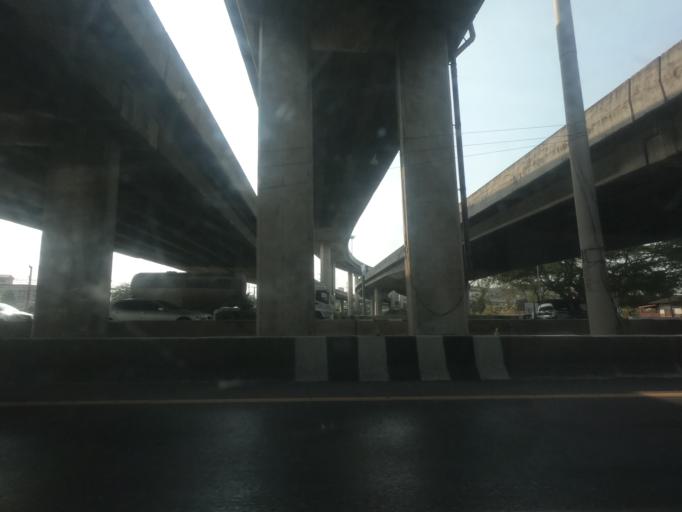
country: TH
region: Pathum Thani
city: Khlong Luang
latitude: 14.0760
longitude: 100.5921
